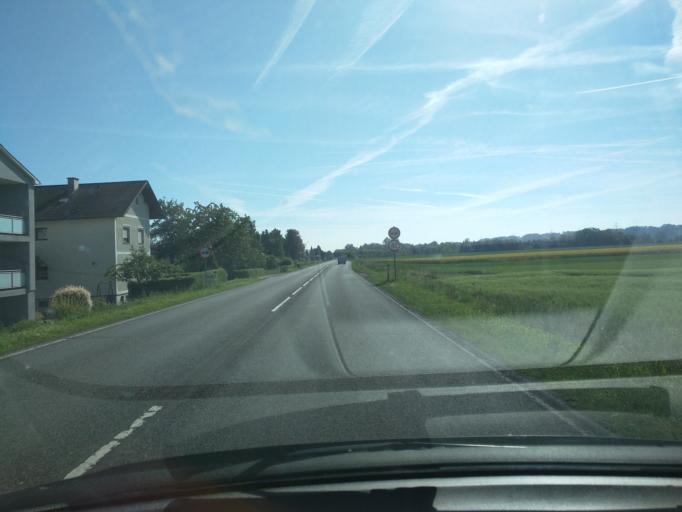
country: AT
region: Lower Austria
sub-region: Politischer Bezirk Amstetten
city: Sankt Georgen am Ybbsfelde
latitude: 48.1156
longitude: 14.9463
